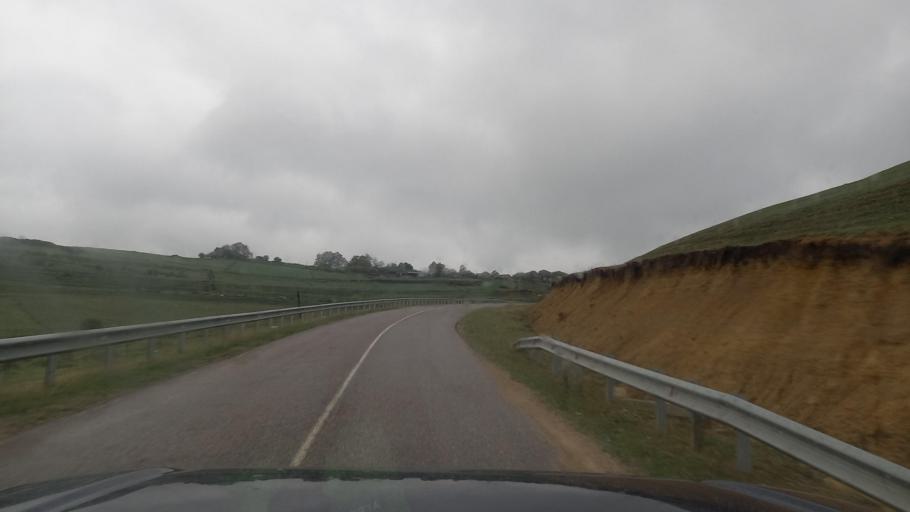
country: RU
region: Stavropol'skiy
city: Nezhinskiy
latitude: 43.8615
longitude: 42.6552
